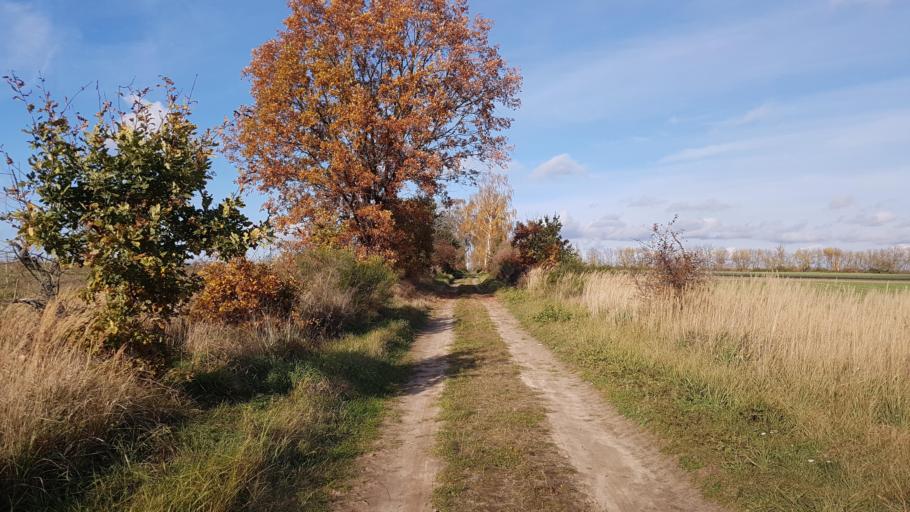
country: DE
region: Saxony-Anhalt
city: Zahna
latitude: 51.9698
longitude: 12.8386
